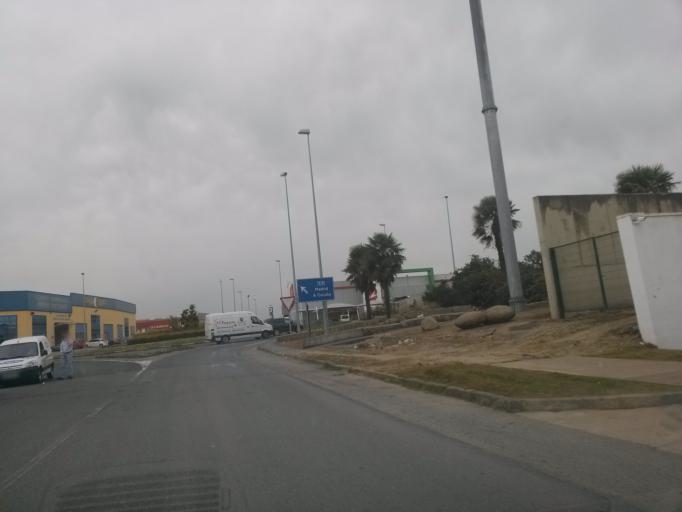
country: ES
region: Galicia
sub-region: Provincia de Lugo
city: Lugo
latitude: 43.0482
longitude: -7.5688
